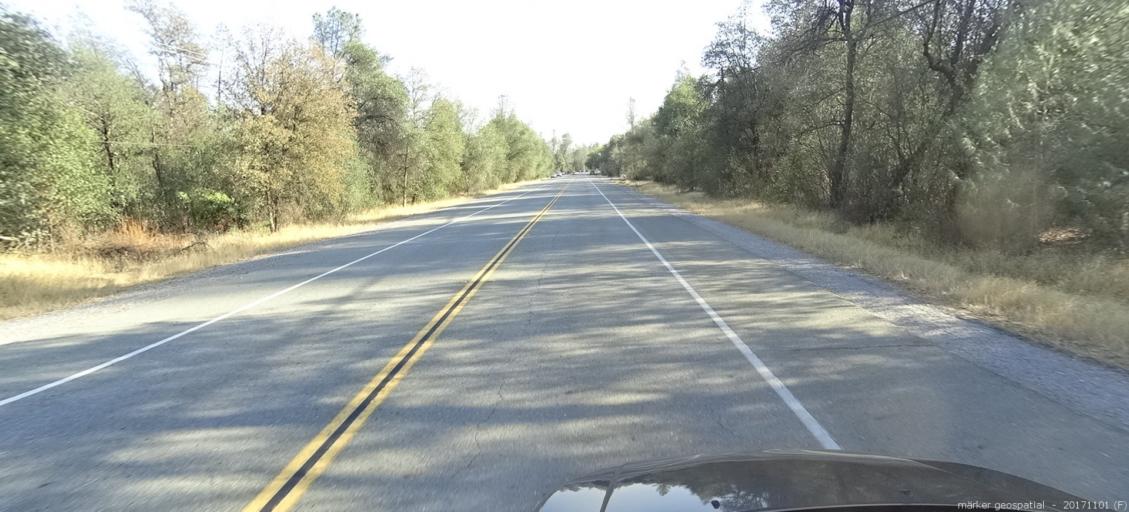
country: US
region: California
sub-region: Shasta County
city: Shasta Lake
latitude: 40.6276
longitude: -122.3228
